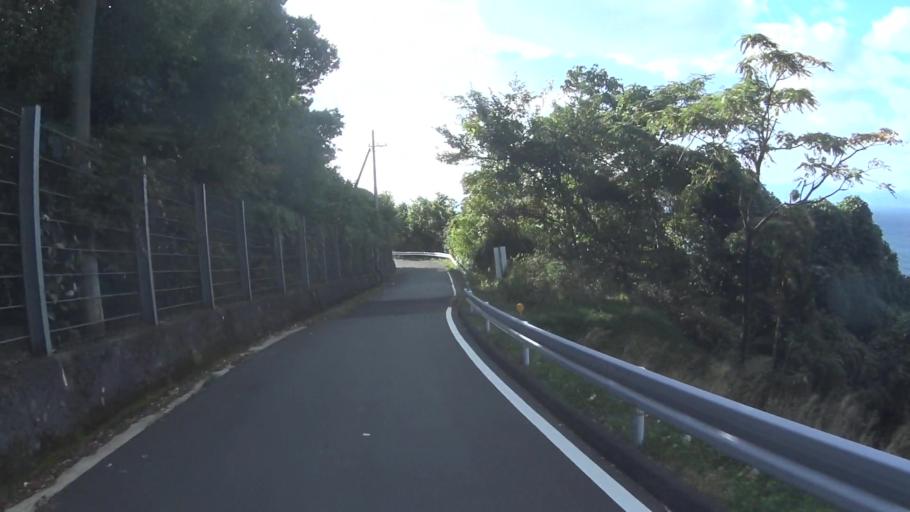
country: JP
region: Kyoto
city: Maizuru
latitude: 35.5667
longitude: 135.4118
